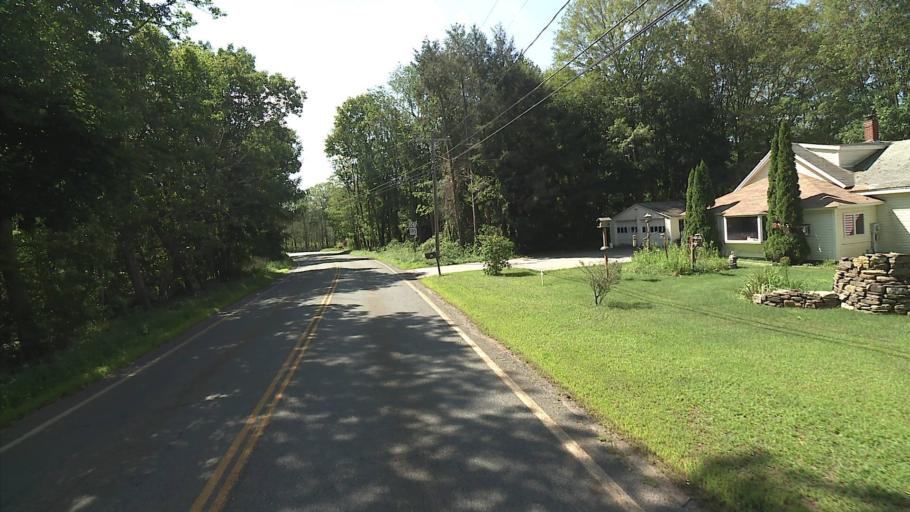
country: US
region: Connecticut
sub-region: Tolland County
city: Mansfield City
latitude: 41.7676
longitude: -72.1962
